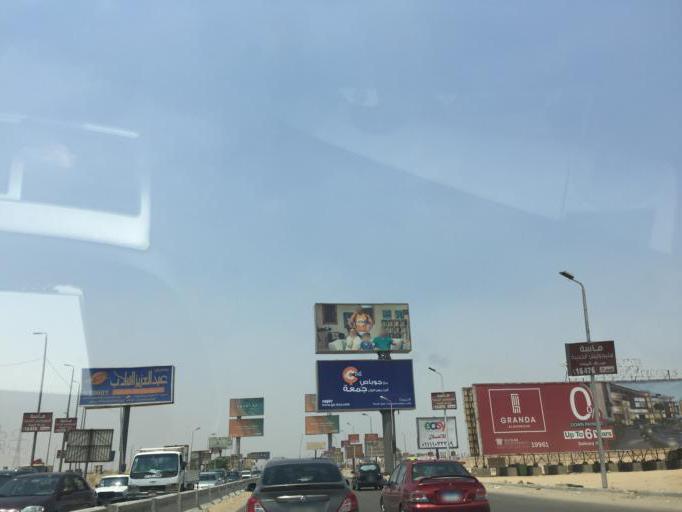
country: EG
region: Muhafazat al Qalyubiyah
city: Al Khankah
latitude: 30.0795
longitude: 31.4340
